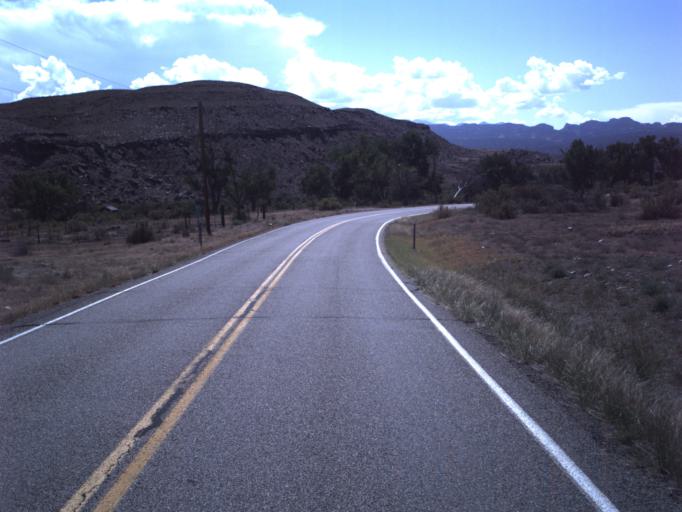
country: US
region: Utah
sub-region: Grand County
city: Moab
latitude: 38.8462
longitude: -109.2823
